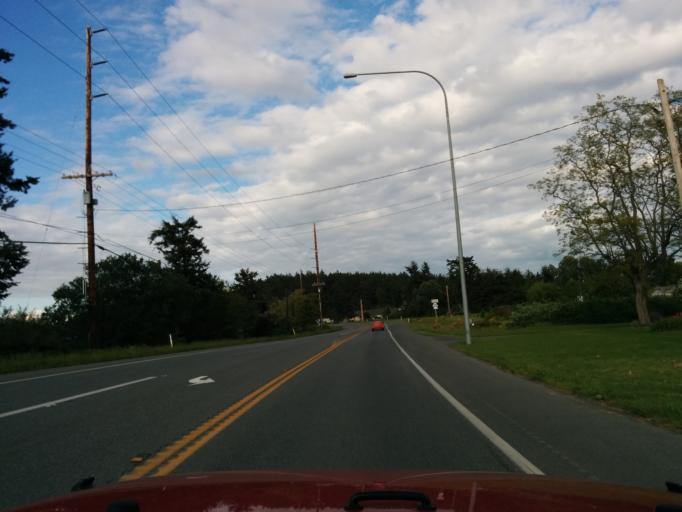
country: US
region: Washington
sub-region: Island County
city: Coupeville
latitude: 48.2646
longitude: -122.6802
